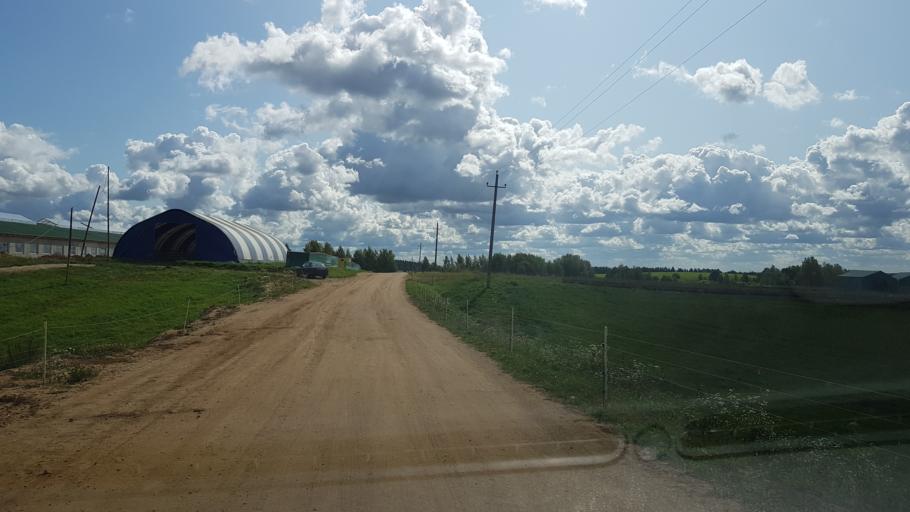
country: BY
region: Minsk
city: Dzyarzhynsk
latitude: 53.7595
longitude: 27.2048
